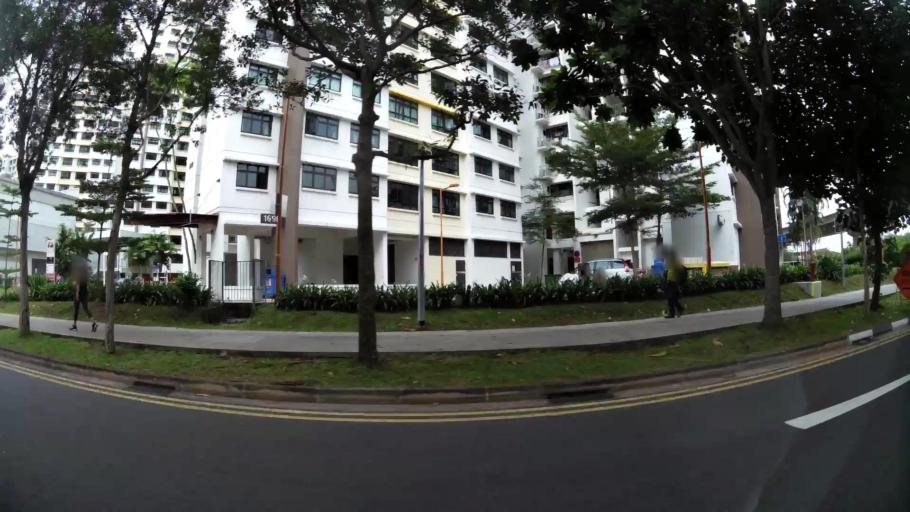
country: MY
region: Johor
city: Kampung Pasir Gudang Baru
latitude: 1.3929
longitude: 103.9140
